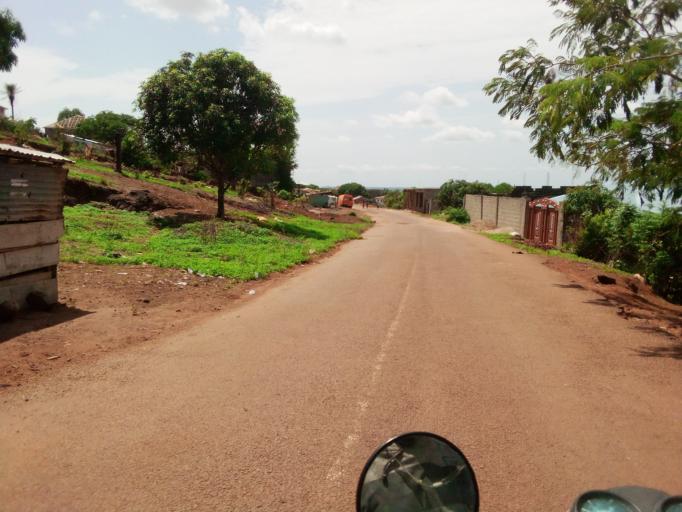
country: SL
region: Western Area
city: Waterloo
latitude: 8.3513
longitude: -13.0790
